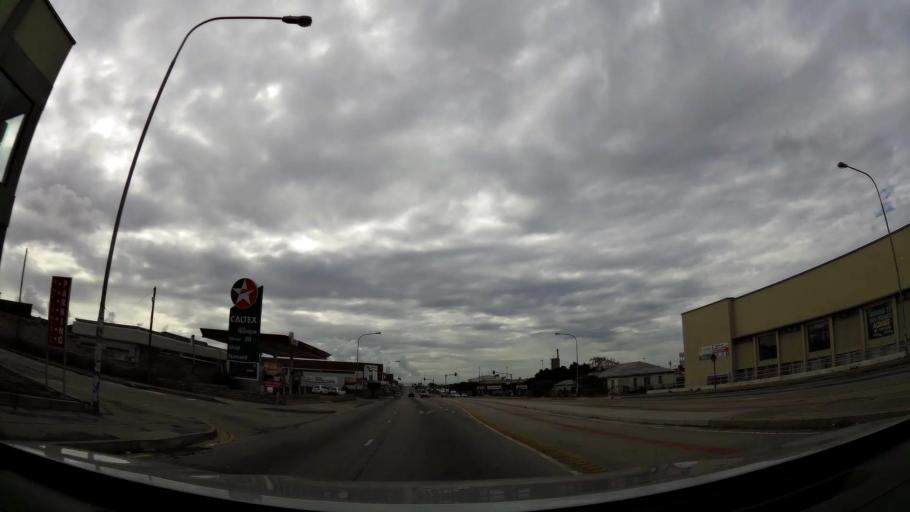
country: ZA
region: Eastern Cape
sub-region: Nelson Mandela Bay Metropolitan Municipality
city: Port Elizabeth
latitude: -33.9358
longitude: 25.5840
